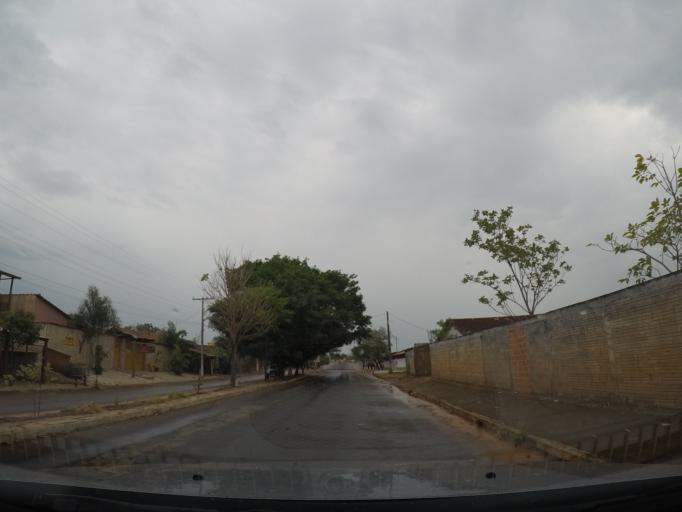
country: BR
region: Goias
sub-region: Pirenopolis
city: Pirenopolis
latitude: -15.8525
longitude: -48.9425
